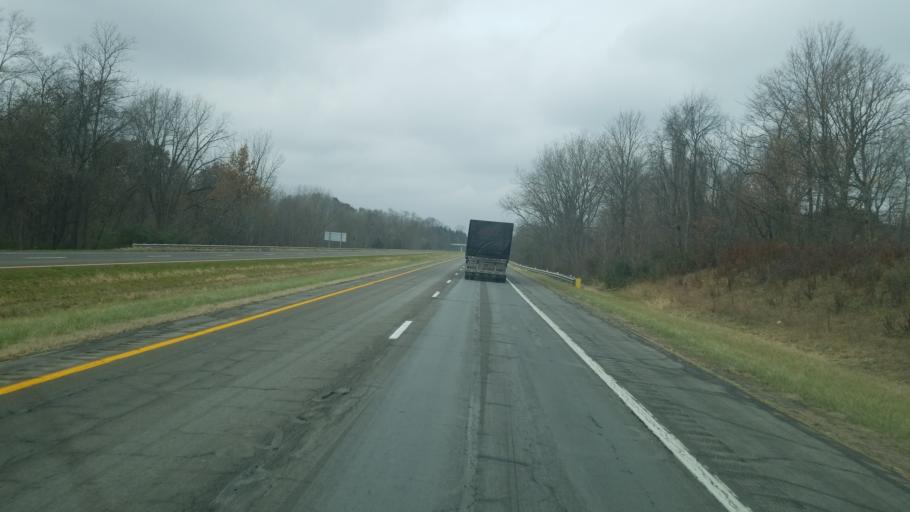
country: US
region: Ohio
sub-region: Huron County
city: Norwalk
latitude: 41.2231
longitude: -82.6243
